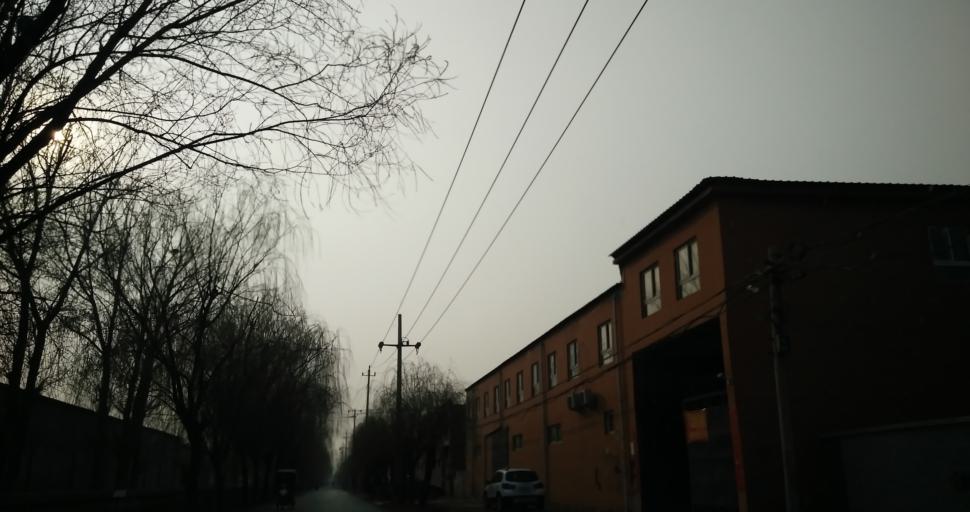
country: CN
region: Beijing
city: Xingfeng
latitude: 39.7081
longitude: 116.3699
